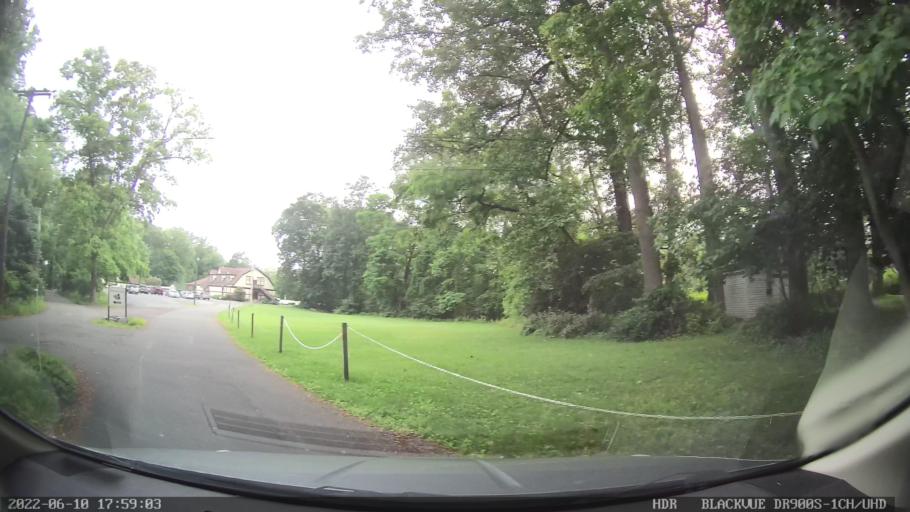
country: US
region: Pennsylvania
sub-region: Berks County
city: Mount Penn
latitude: 40.3402
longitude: -75.8920
